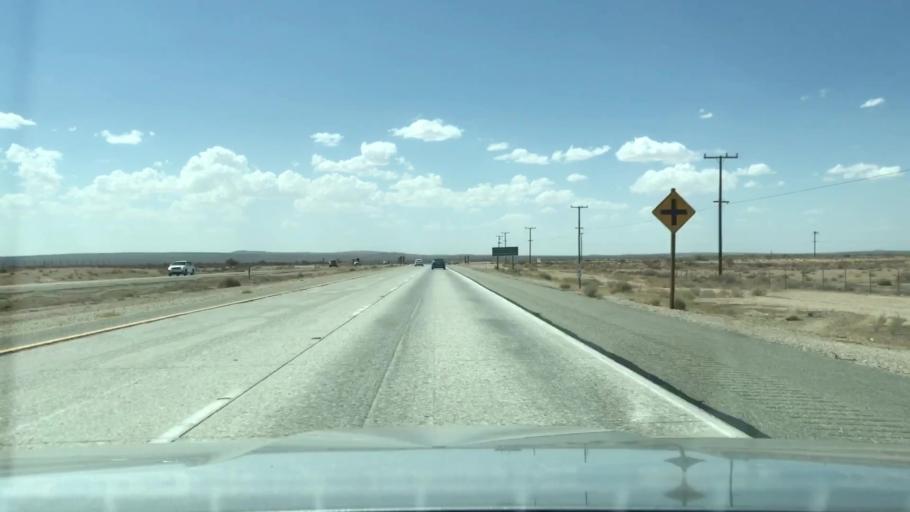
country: US
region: California
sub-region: San Bernardino County
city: Lenwood
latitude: 34.9245
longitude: -117.3262
